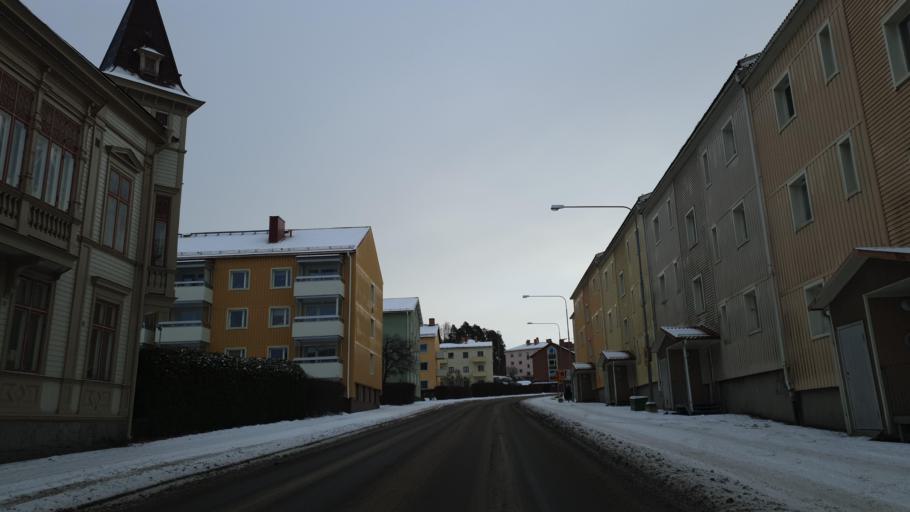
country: SE
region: Gaevleborg
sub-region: Soderhamns Kommun
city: Soderhamn
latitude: 61.2997
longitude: 17.0550
